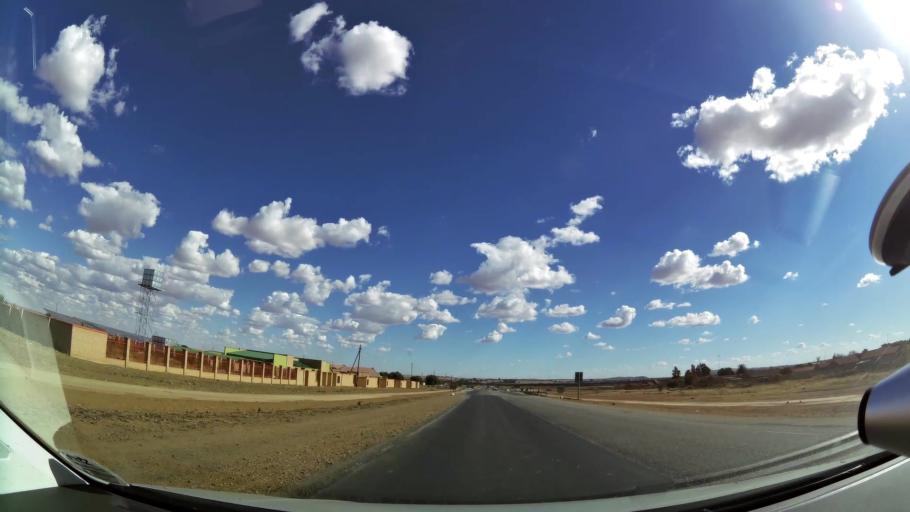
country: ZA
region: North-West
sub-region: Dr Kenneth Kaunda District Municipality
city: Klerksdorp
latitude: -26.8773
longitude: 26.5853
